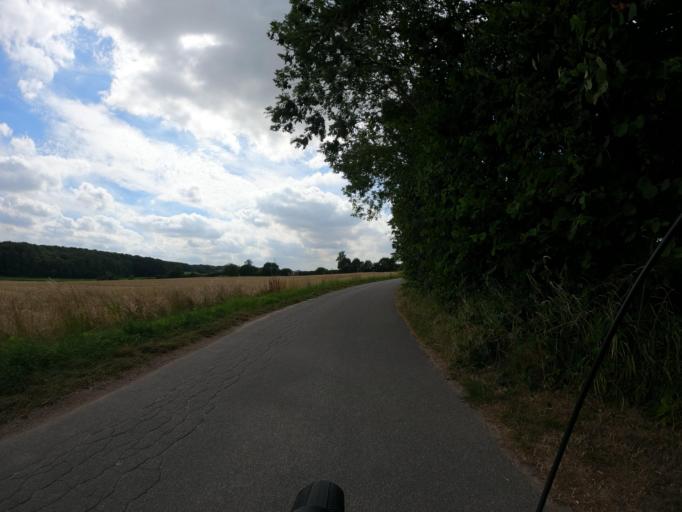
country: DE
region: Schleswig-Holstein
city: Steinberg
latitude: 54.7948
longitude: 9.7902
